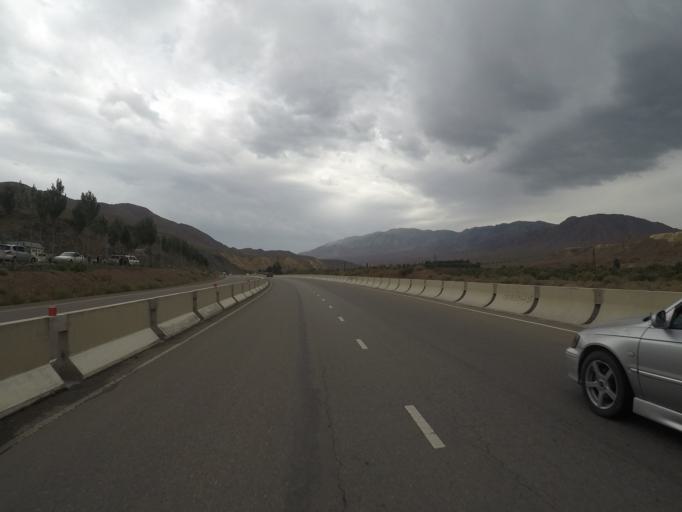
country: KG
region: Naryn
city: Kochkor
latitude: 42.4966
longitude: 75.8439
